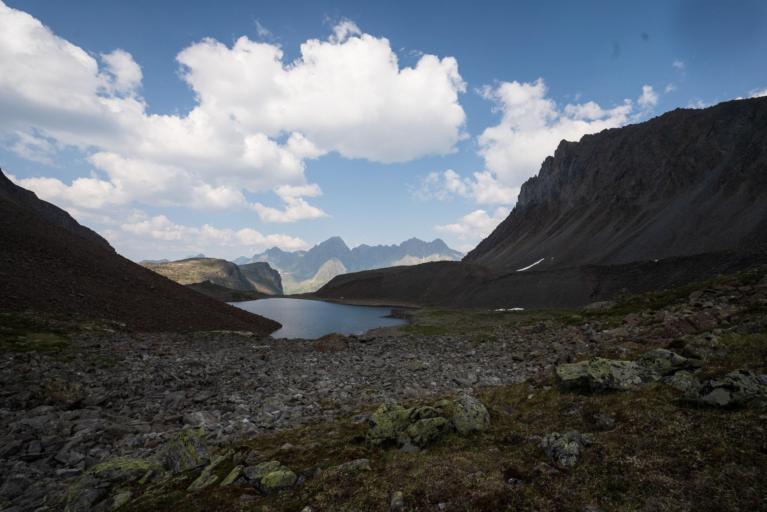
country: RU
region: Transbaikal Territory
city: Chara
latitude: 56.8428
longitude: 117.1916
